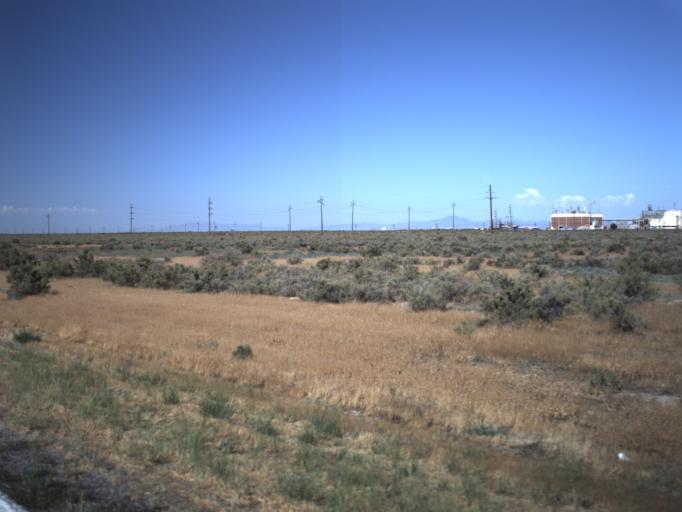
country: US
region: Utah
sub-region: Millard County
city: Delta
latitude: 39.4673
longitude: -112.4274
